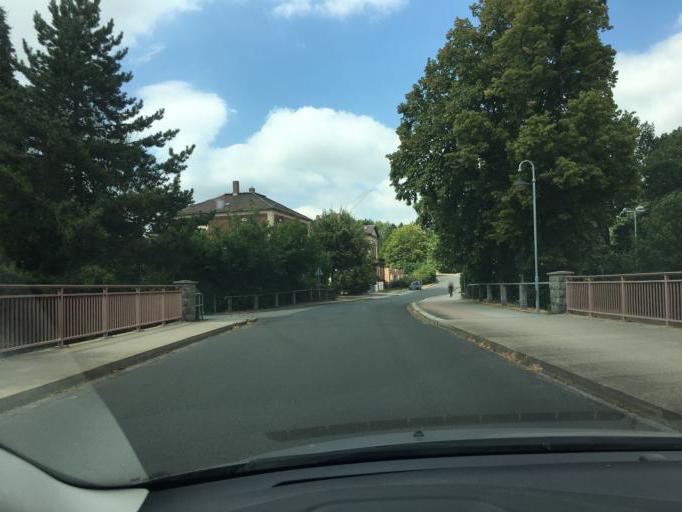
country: DE
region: Saxony
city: Frohburg
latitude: 51.0596
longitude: 12.5570
